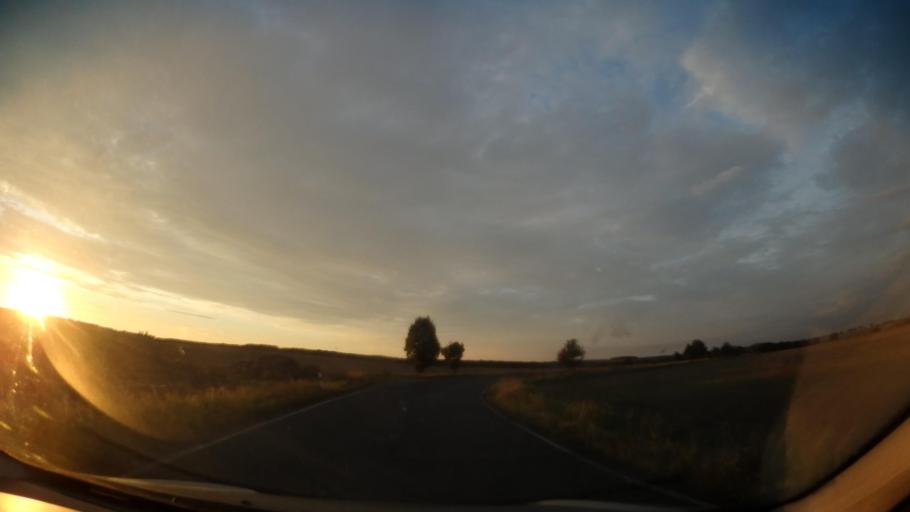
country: CZ
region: Central Bohemia
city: Loucen
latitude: 50.2503
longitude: 15.0223
